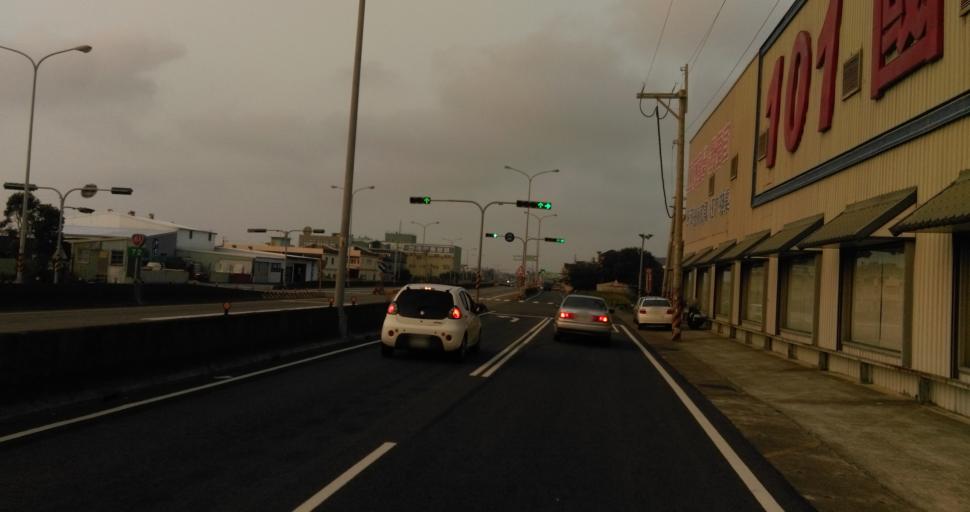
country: TW
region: Taiwan
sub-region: Hsinchu
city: Zhubei
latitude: 24.8661
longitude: 120.9532
